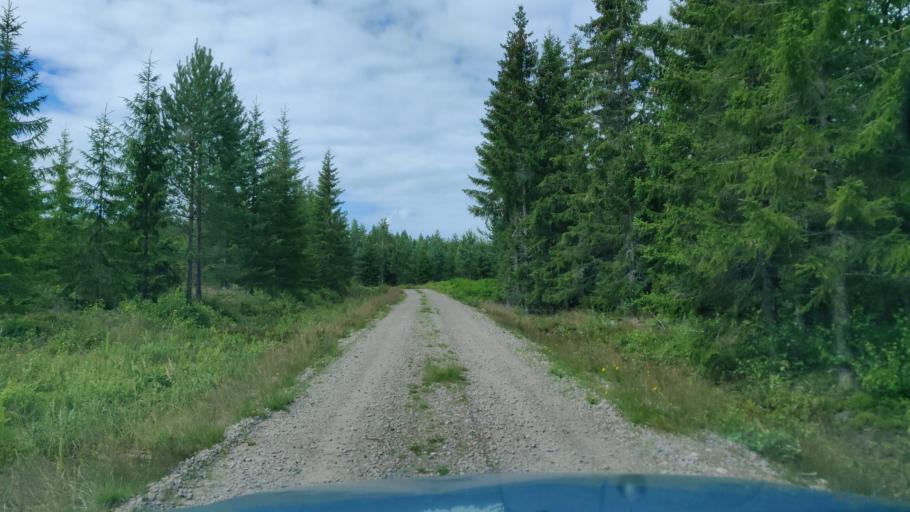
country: SE
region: Vaermland
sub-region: Hagfors Kommun
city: Hagfors
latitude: 59.9469
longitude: 13.5961
